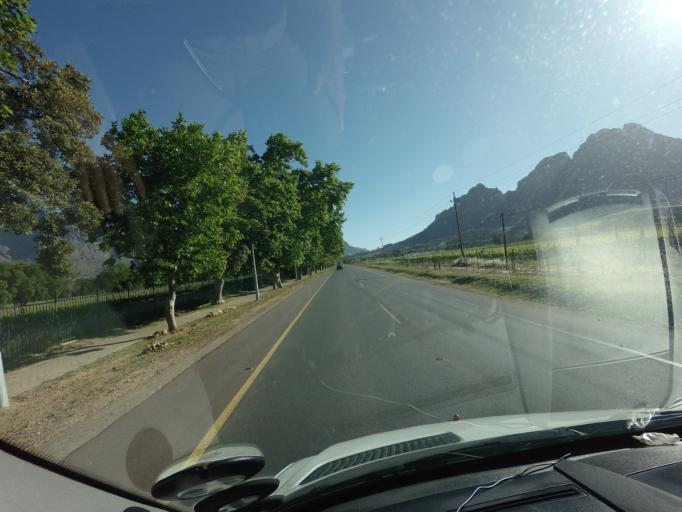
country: ZA
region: Western Cape
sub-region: Cape Winelands District Municipality
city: Stellenbosch
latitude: -33.8791
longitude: 18.9717
